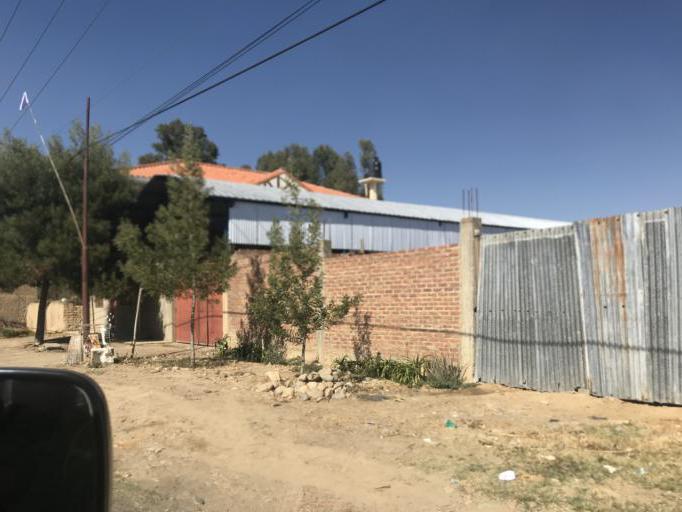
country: BO
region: Cochabamba
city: Punata
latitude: -17.5594
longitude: -65.8696
